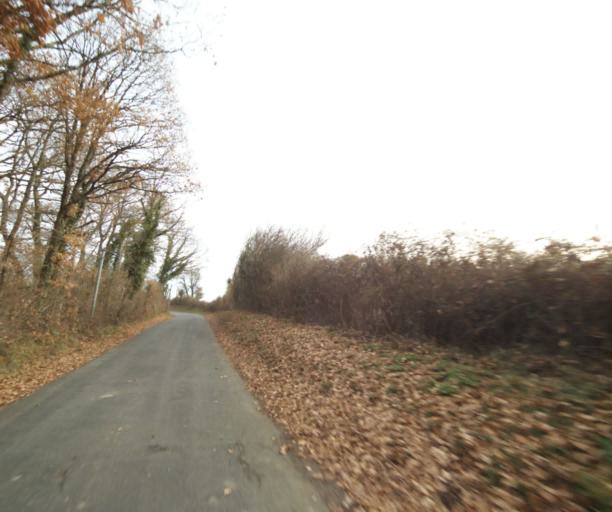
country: FR
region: Poitou-Charentes
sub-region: Departement de la Charente-Maritime
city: Fontcouverte
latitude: 45.7970
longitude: -0.5937
